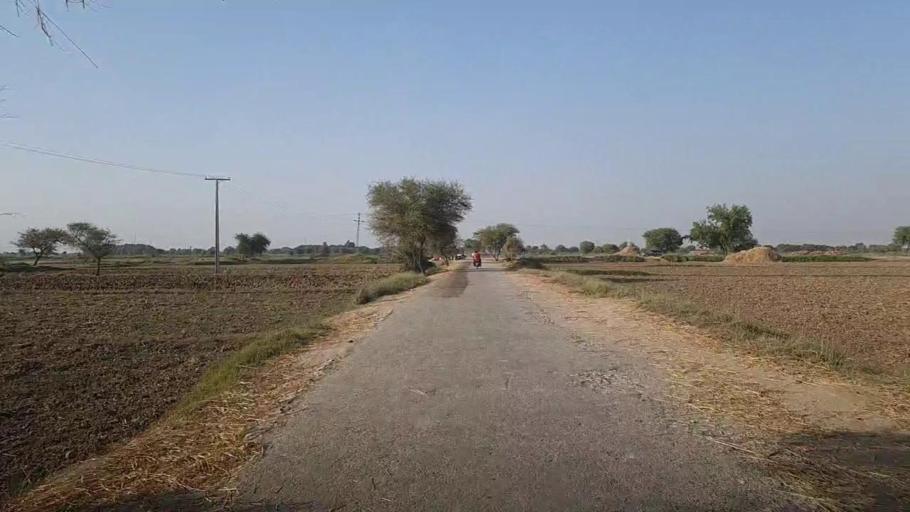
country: PK
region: Sindh
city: Kashmor
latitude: 28.4164
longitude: 69.4104
